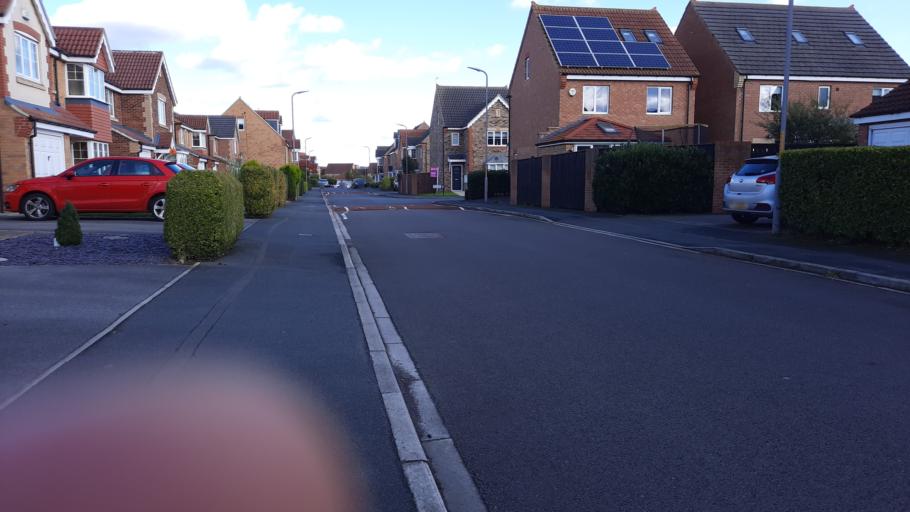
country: GB
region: England
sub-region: Stockton-on-Tees
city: Eaglescliffe
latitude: 54.5262
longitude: -1.3263
